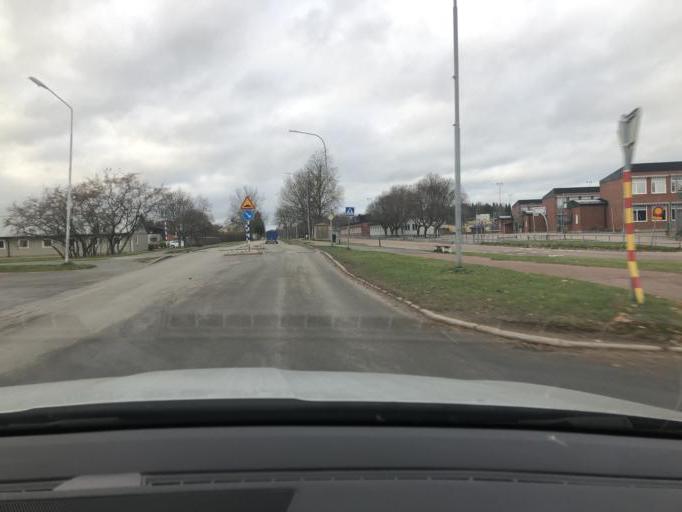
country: SE
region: Uppsala
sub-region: Tierps Kommun
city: Tierp
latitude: 60.3444
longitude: 17.5070
